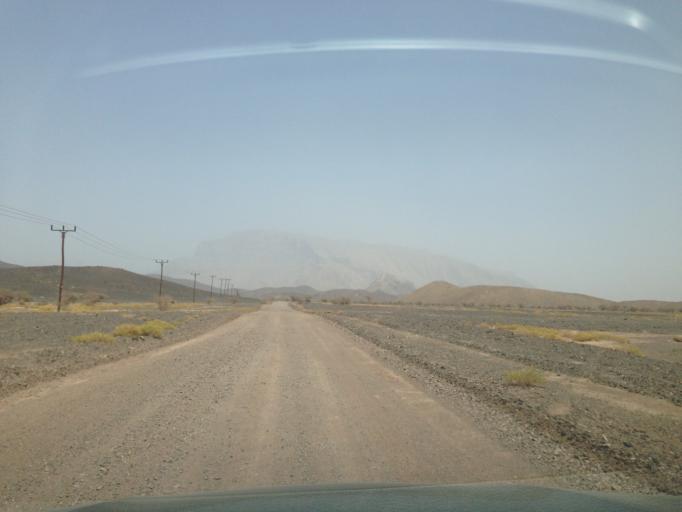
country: OM
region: Az Zahirah
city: `Ibri
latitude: 23.2097
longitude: 56.8416
